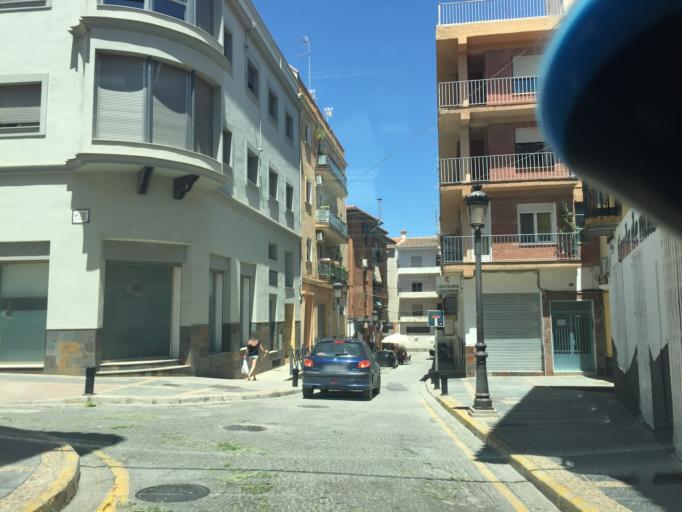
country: ES
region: Andalusia
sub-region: Provincia de Granada
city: Guadix
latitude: 37.3008
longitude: -3.1340
